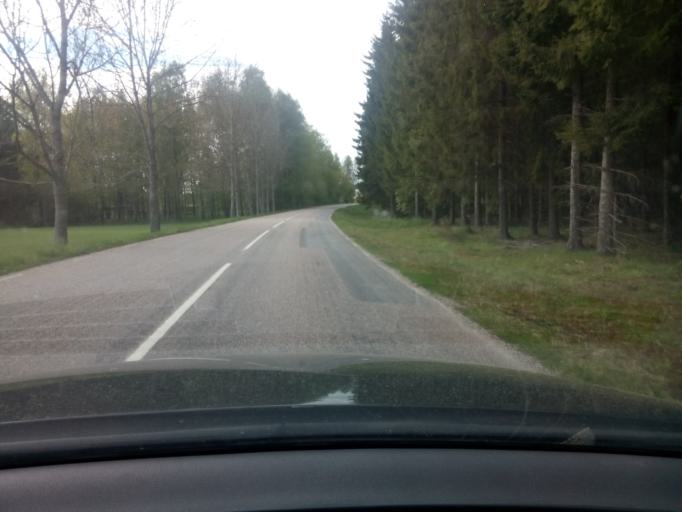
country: SE
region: Soedermanland
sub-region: Nykopings Kommun
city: Nykoping
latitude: 58.8424
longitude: 16.9326
